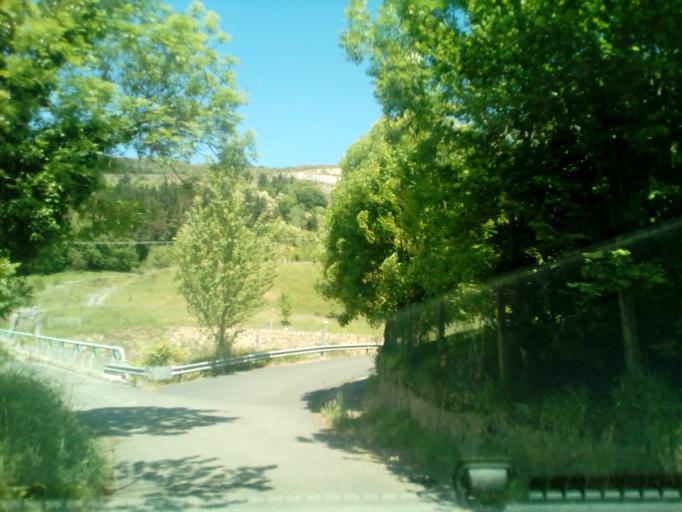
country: ES
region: Basque Country
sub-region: Provincia de Guipuzcoa
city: Andoain
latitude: 43.2272
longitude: -2.0159
